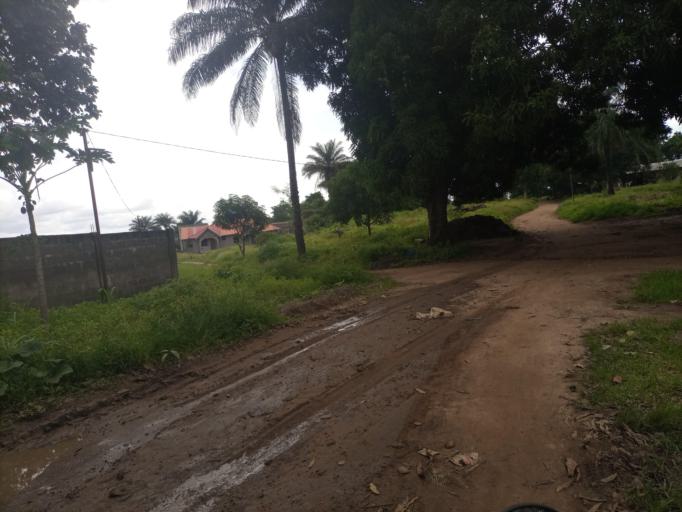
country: SL
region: Northern Province
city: Masoyila
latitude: 8.5698
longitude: -13.1611
